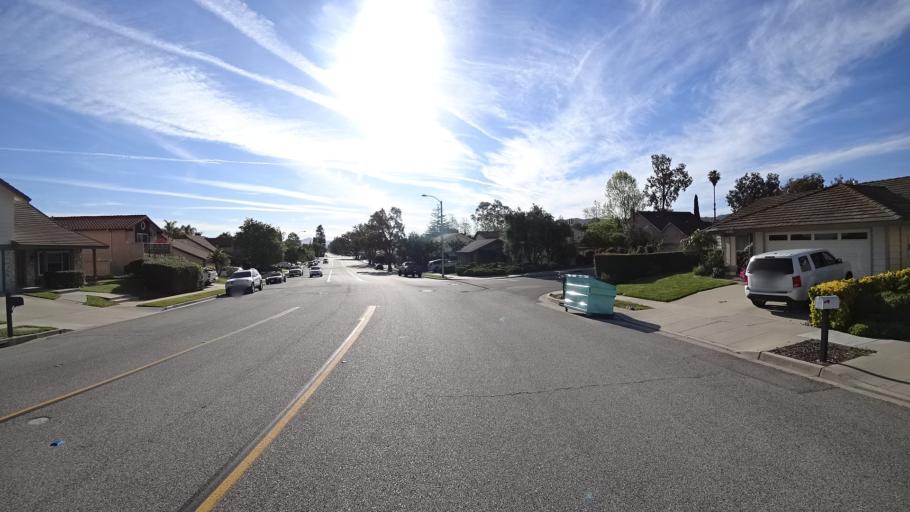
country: US
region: California
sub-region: Ventura County
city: Casa Conejo
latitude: 34.1861
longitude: -118.9569
